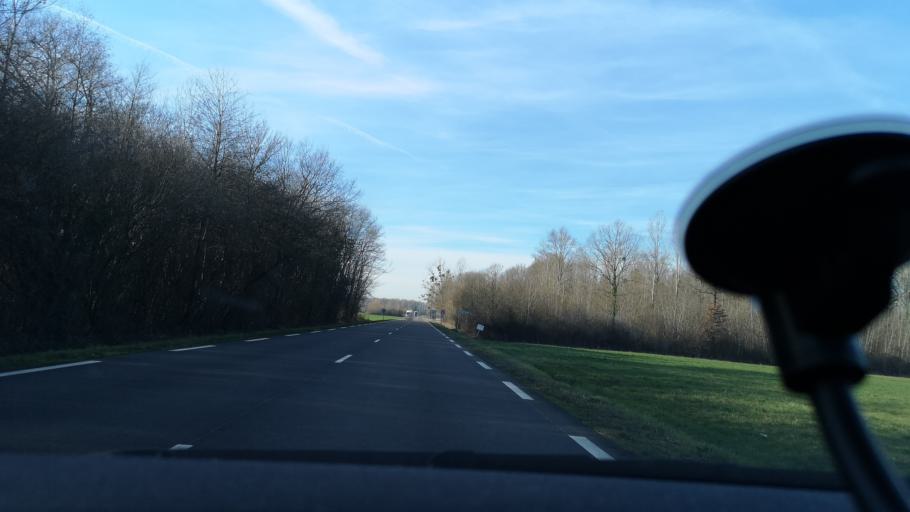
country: FR
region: Bourgogne
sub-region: Departement de la Cote-d'Or
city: Seurre
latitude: 46.9626
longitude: 5.1840
